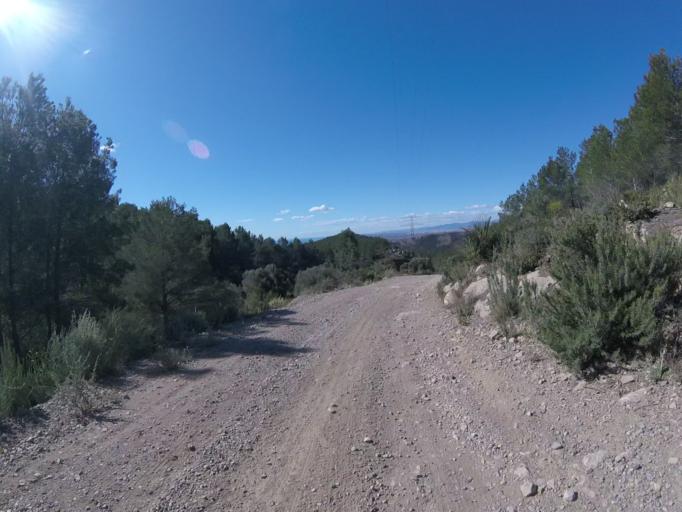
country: ES
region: Valencia
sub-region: Provincia de Castello
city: Benicassim
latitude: 40.0809
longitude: 0.0821
